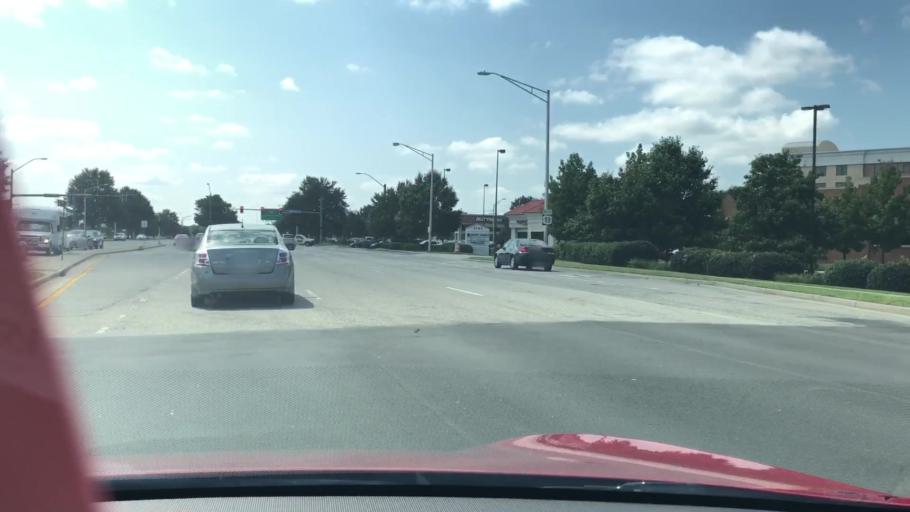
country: US
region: Virginia
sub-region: City of Norfolk
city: Norfolk
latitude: 36.8628
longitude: -76.2105
